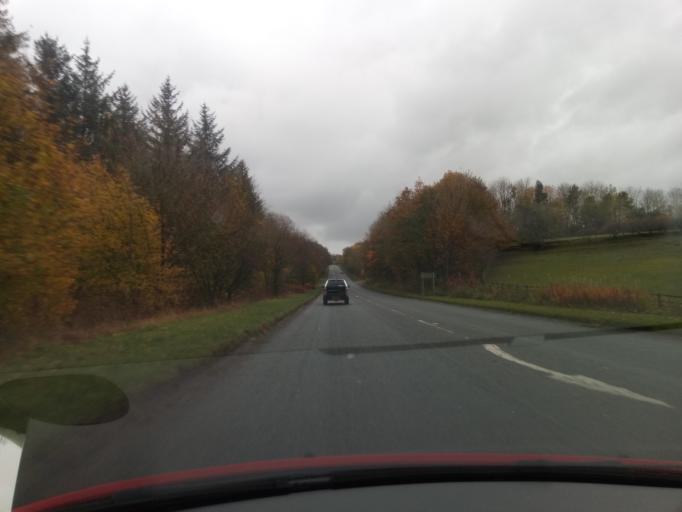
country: GB
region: England
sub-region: County Durham
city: High Etherley
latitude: 54.6662
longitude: -1.7730
